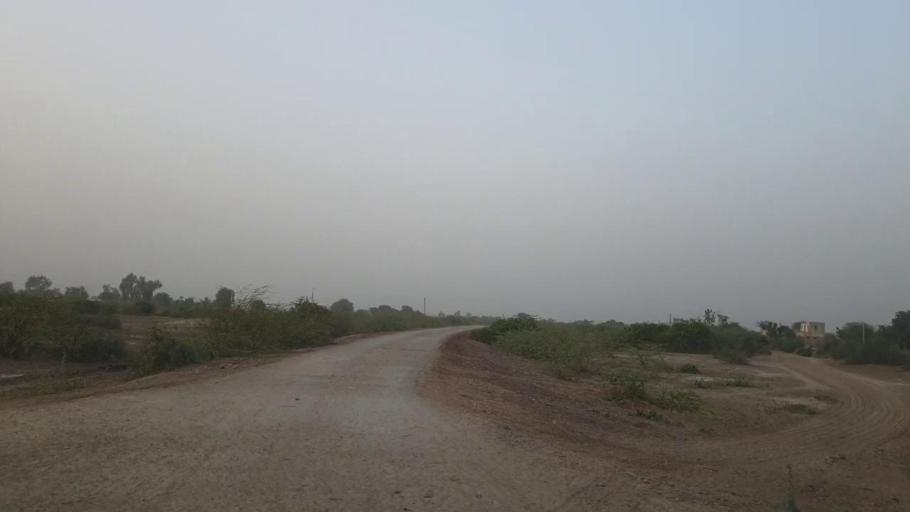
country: PK
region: Sindh
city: Kunri
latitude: 25.1250
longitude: 69.5589
